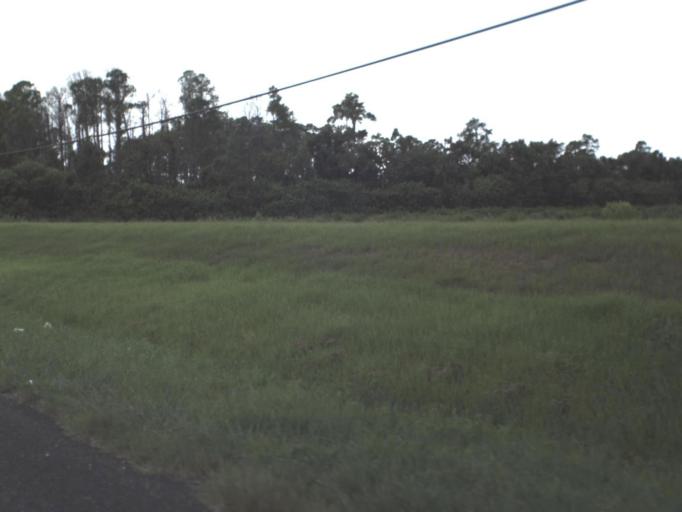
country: US
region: Florida
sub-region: Hillsborough County
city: Sun City Center
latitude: 27.7640
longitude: -82.3351
